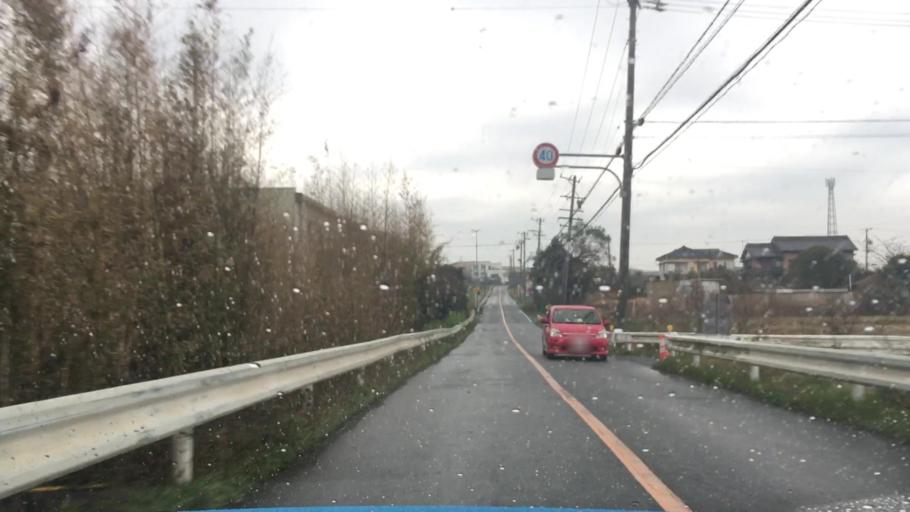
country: JP
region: Aichi
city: Toyohashi
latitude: 34.6858
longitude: 137.3903
